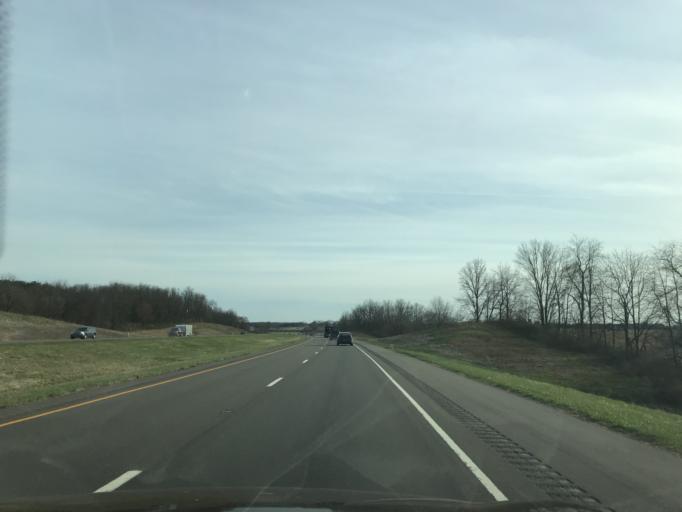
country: US
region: Pennsylvania
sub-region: Northumberland County
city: Watsontown
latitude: 41.1088
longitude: -76.8063
